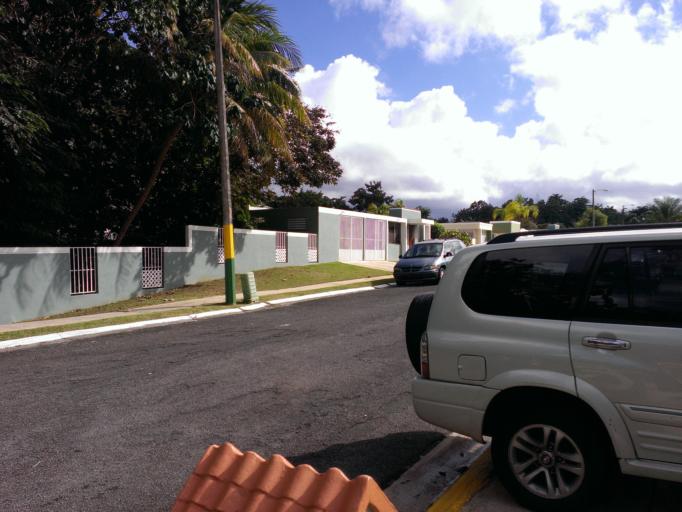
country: PR
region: Toa Baja
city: Candelaria
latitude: 18.3979
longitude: -66.1963
